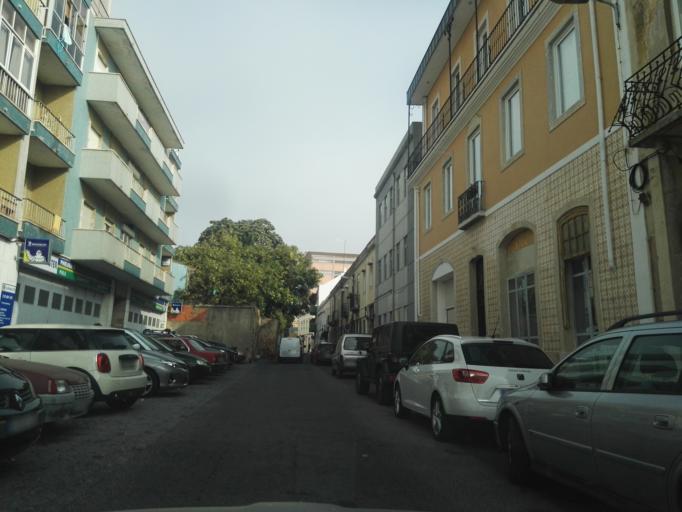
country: PT
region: Lisbon
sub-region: Loures
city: Moscavide
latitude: 38.7462
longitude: -9.1014
